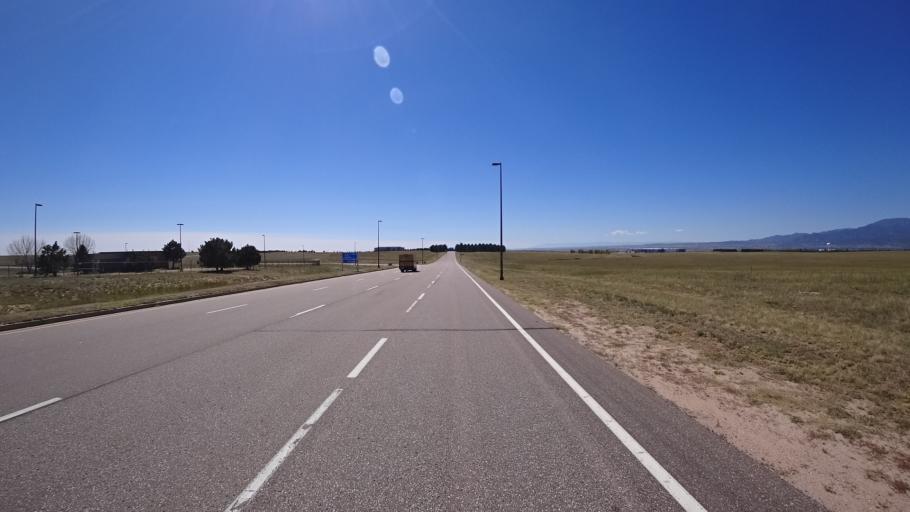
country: US
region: Colorado
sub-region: El Paso County
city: Security-Widefield
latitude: 38.7905
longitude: -104.7043
